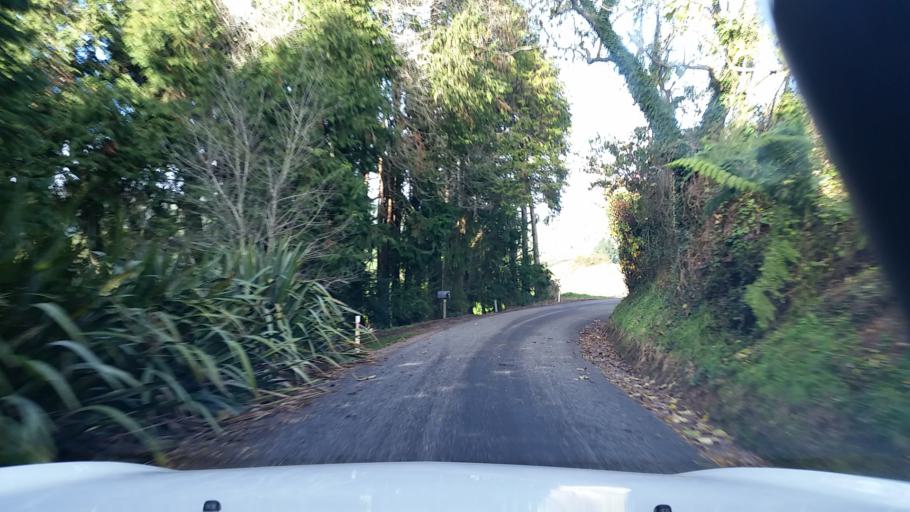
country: NZ
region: Waikato
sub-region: Matamata-Piako District
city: Matamata
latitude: -37.8060
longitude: 175.6353
